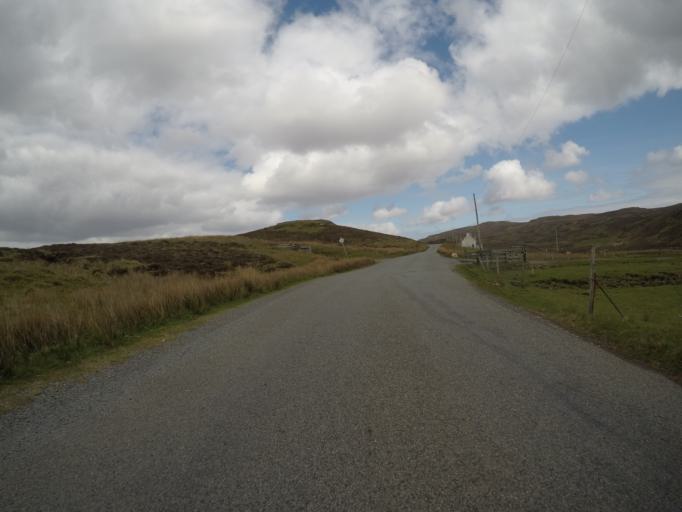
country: GB
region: Scotland
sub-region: Highland
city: Isle of Skye
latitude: 57.3743
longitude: -6.3758
